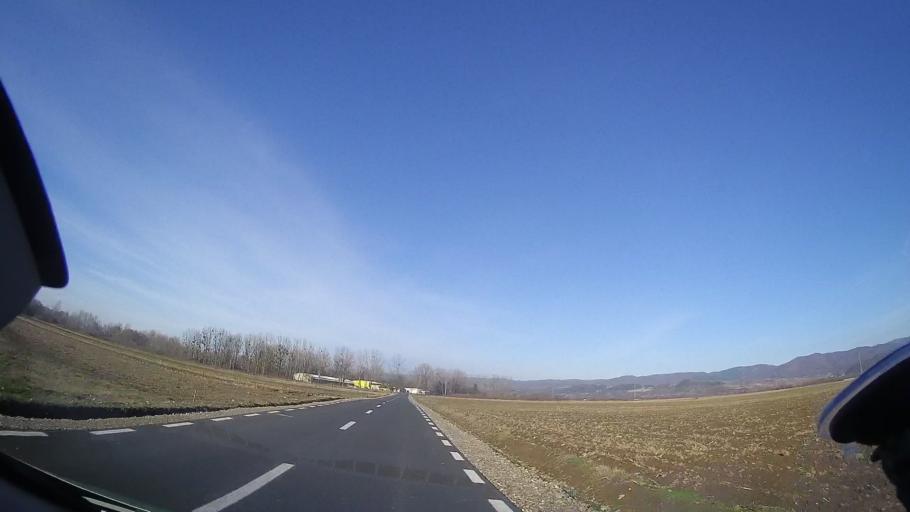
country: RO
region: Bihor
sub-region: Comuna Vadu Crisului
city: Vadu Crisului
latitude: 47.0014
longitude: 22.5033
